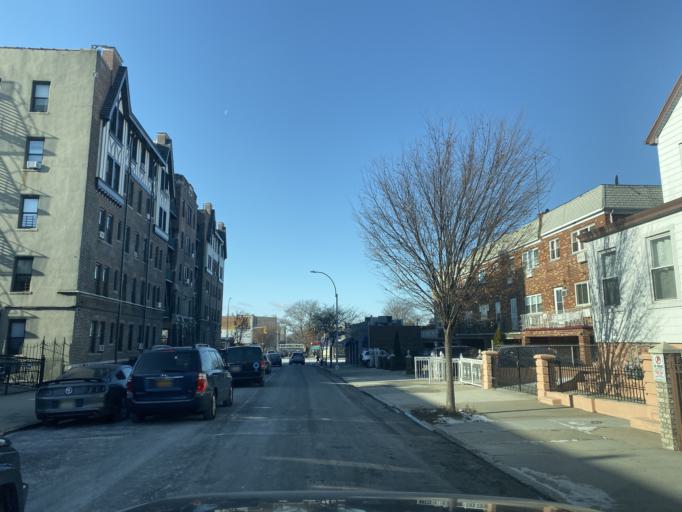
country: US
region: New York
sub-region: Bronx
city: The Bronx
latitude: 40.8314
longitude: -73.8498
